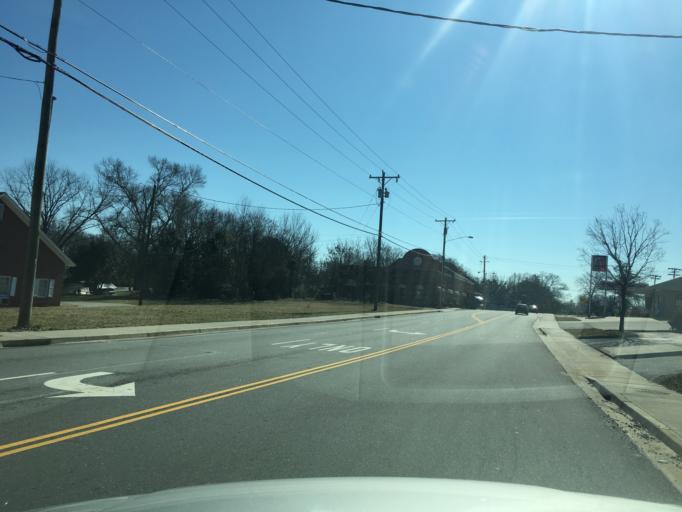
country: US
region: South Carolina
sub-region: Pickens County
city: Liberty
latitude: 34.7878
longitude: -82.6928
